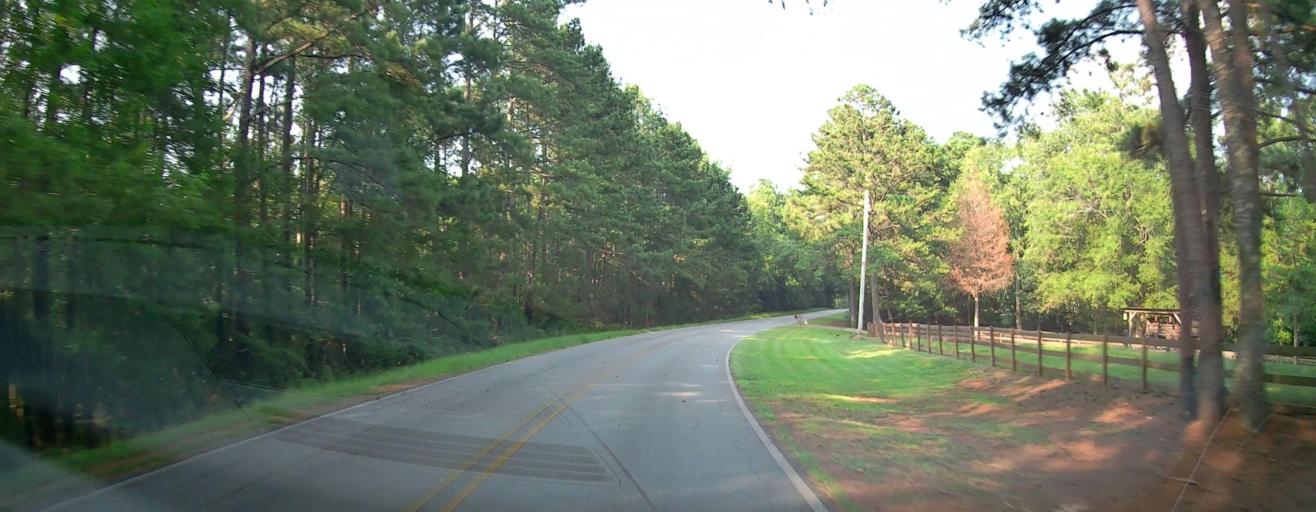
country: US
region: Georgia
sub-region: Monroe County
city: Forsyth
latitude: 32.9951
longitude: -83.7740
